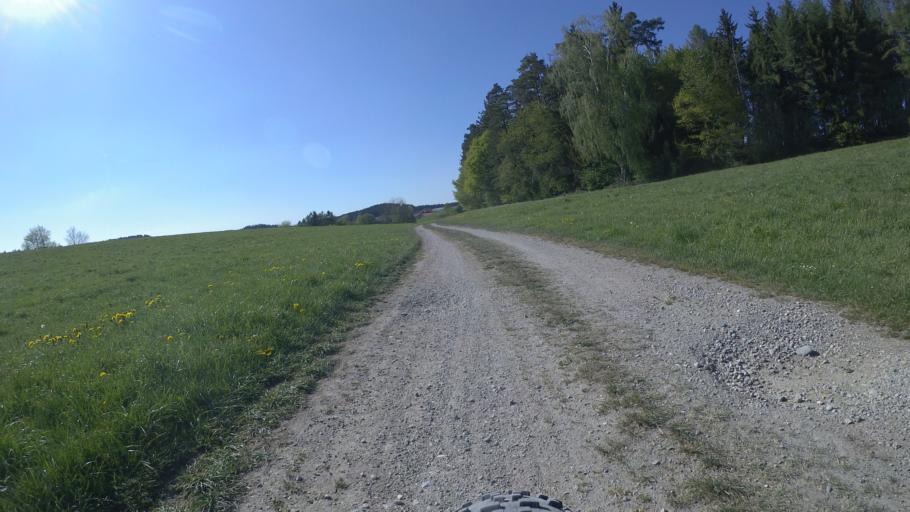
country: DE
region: Bavaria
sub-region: Upper Bavaria
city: Traunreut
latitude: 47.9413
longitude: 12.5536
